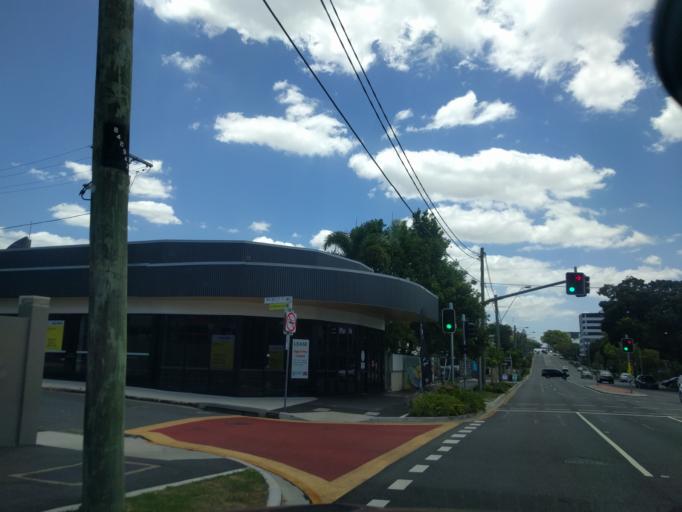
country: AU
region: Queensland
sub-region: Brisbane
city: Woolloongabba
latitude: -27.4815
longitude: 153.0357
